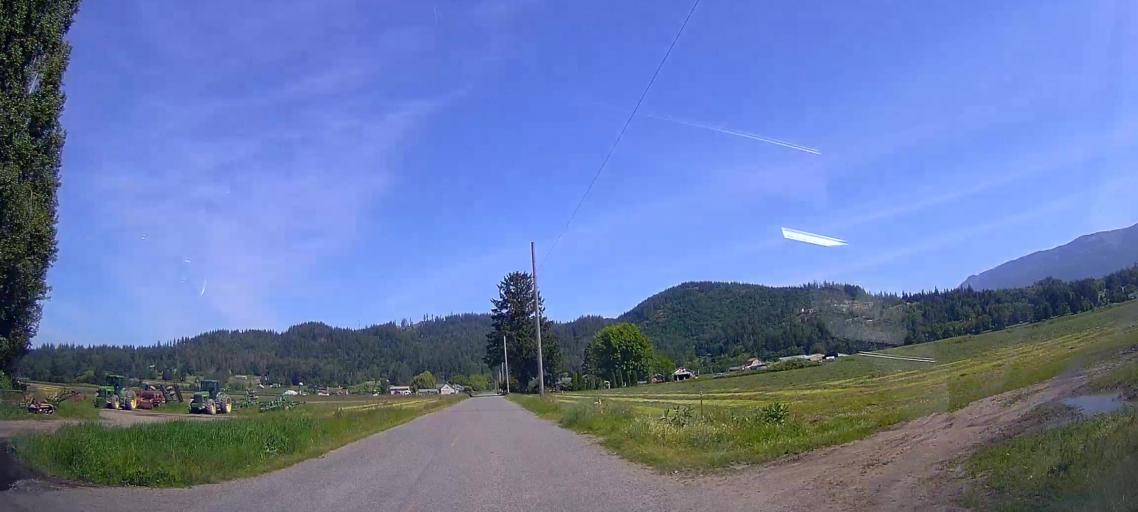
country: US
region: Washington
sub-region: Skagit County
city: Sedro-Woolley
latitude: 48.5241
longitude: -122.2907
